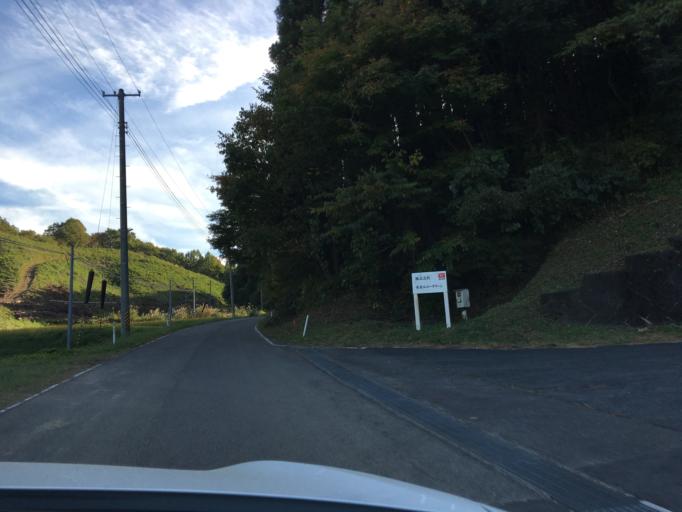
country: JP
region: Fukushima
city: Ishikawa
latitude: 37.2539
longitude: 140.6074
